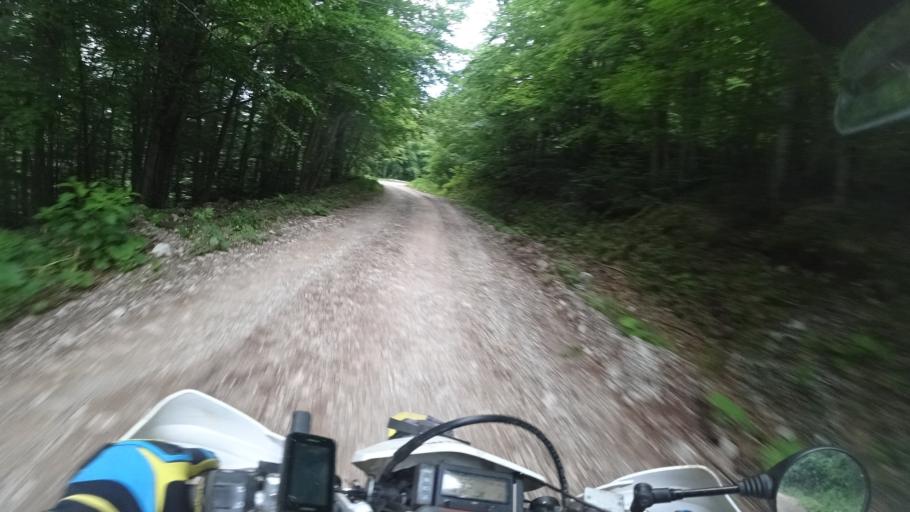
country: HR
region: Licko-Senjska
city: Gospic
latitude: 44.4664
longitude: 15.2995
